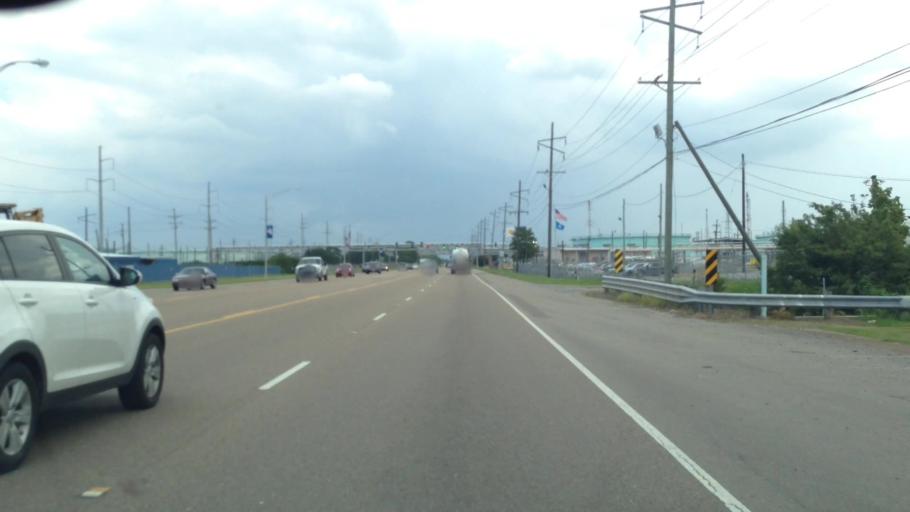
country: US
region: Louisiana
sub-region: Saint Charles Parish
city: Norco
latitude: 30.0142
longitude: -90.4054
